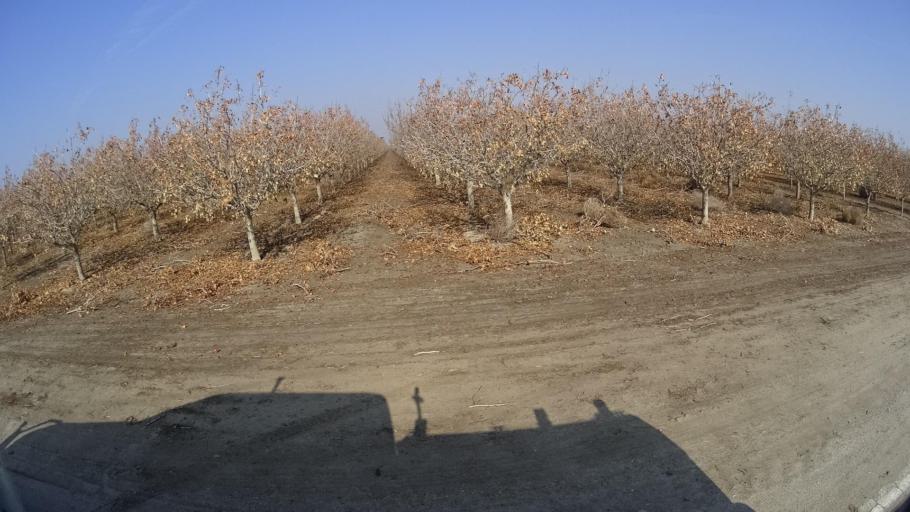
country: US
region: California
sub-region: Kern County
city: Buttonwillow
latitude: 35.3404
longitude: -119.3770
